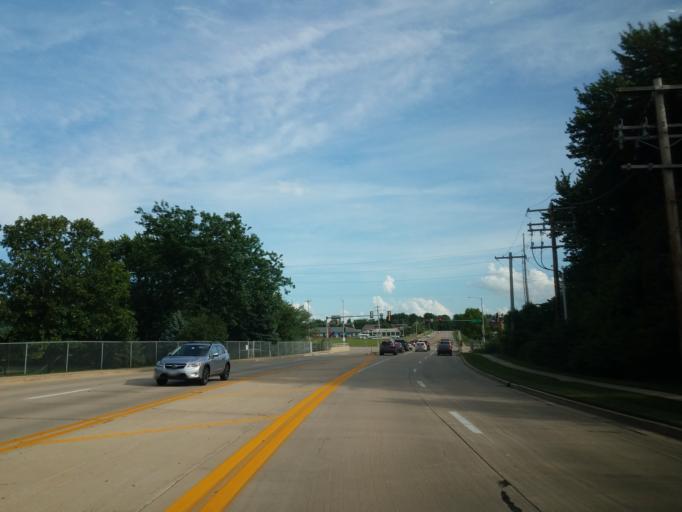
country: US
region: Illinois
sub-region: McLean County
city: Normal
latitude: 40.5038
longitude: -88.9388
